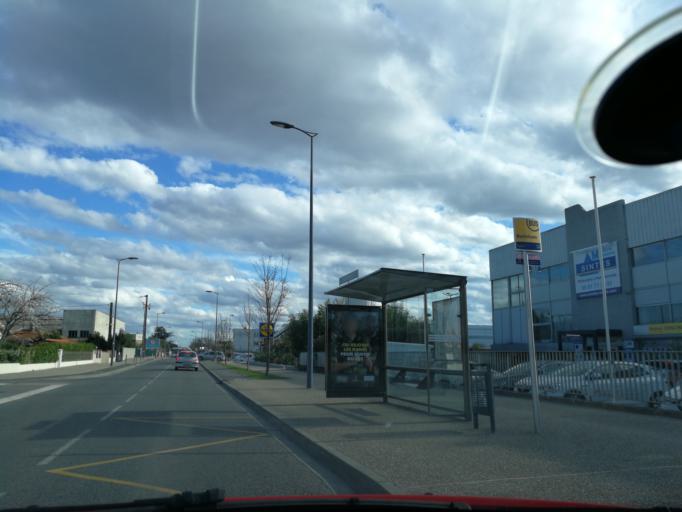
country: FR
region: Midi-Pyrenees
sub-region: Departement de la Haute-Garonne
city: Beauzelle
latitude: 43.6490
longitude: 1.3825
